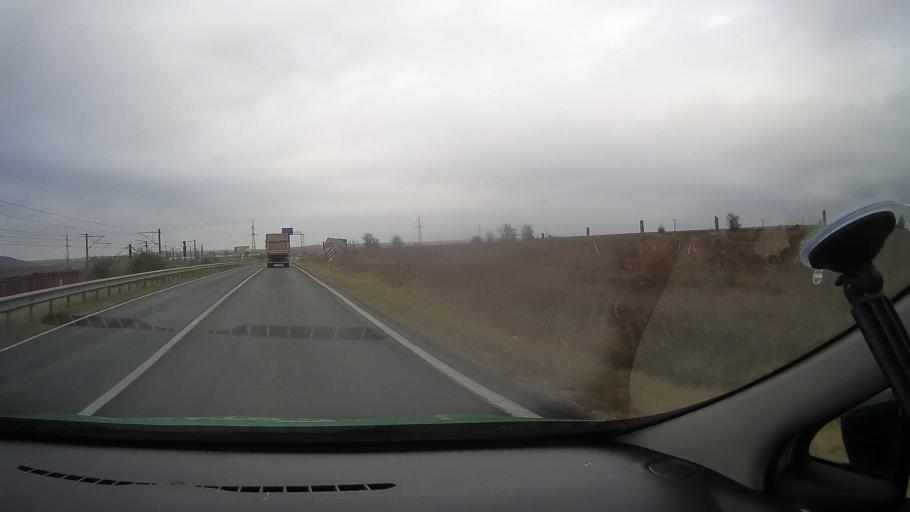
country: RO
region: Constanta
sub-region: Comuna Poarta Alba
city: Poarta Alba
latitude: 44.2315
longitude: 28.3776
